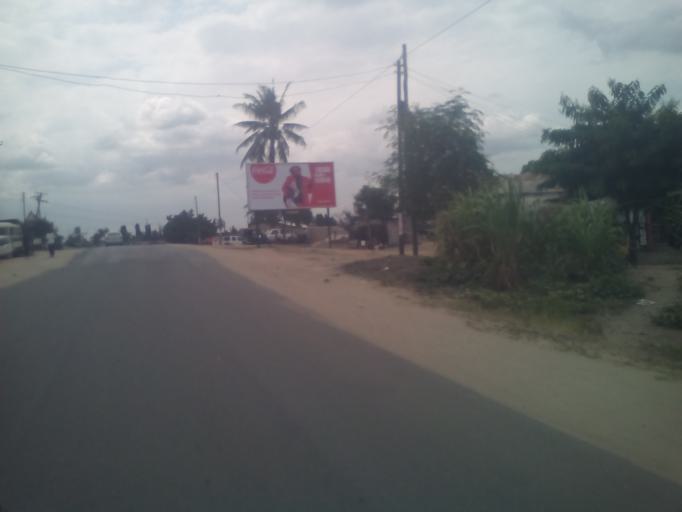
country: TZ
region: Dar es Salaam
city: Dar es Salaam
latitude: -6.8724
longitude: 39.2233
